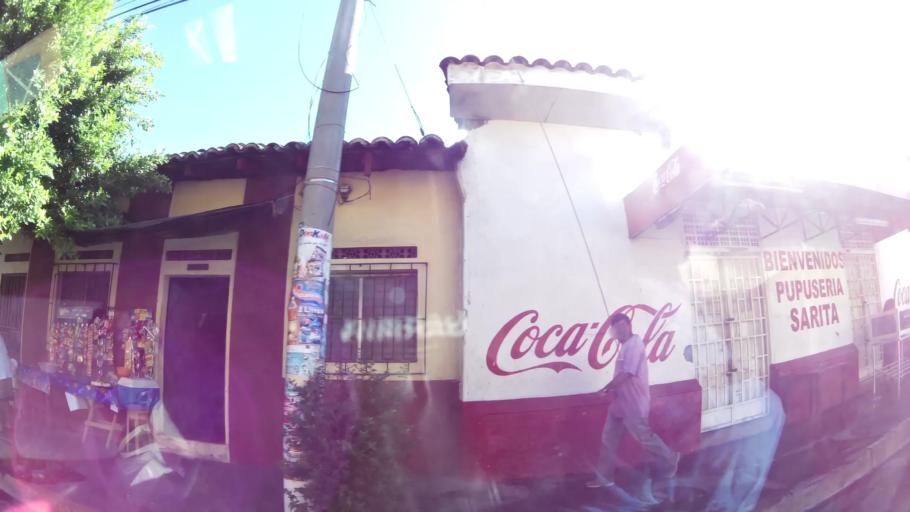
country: SV
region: San Miguel
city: San Miguel
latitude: 13.4779
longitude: -88.1806
